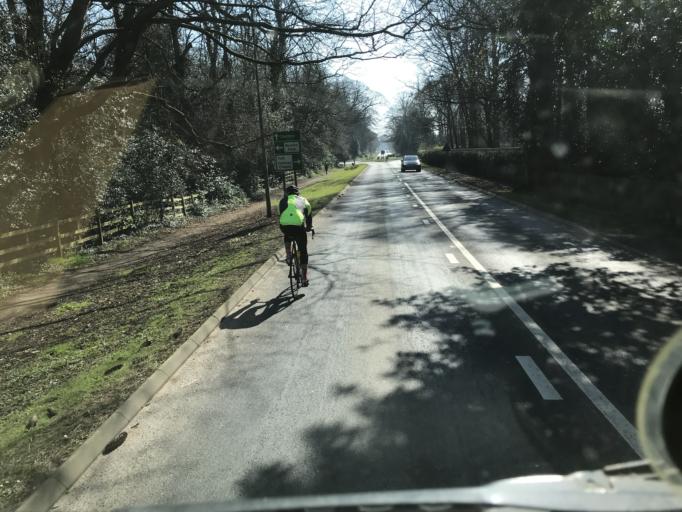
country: GB
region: England
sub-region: Cheshire East
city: Knutsford
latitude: 53.2953
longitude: -2.3565
